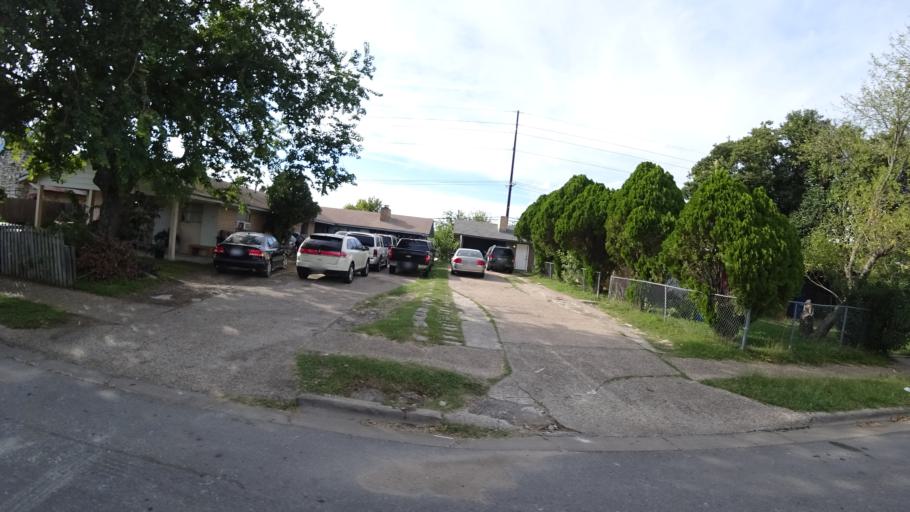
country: US
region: Texas
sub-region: Travis County
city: Onion Creek
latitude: 30.1975
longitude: -97.7560
